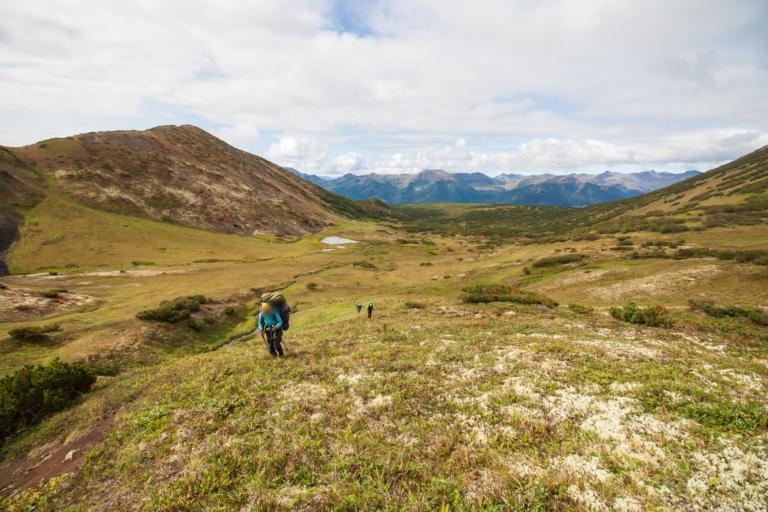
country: RU
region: Kamtsjatka
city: Yelizovo
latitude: 53.8316
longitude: 158.1620
